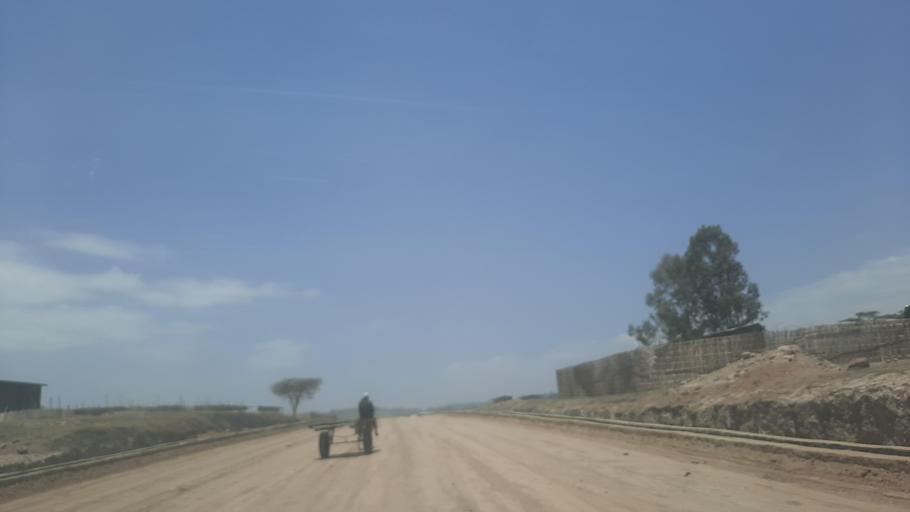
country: ET
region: Southern Nations, Nationalities, and People's Region
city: Butajira
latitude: 7.8453
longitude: 38.1756
